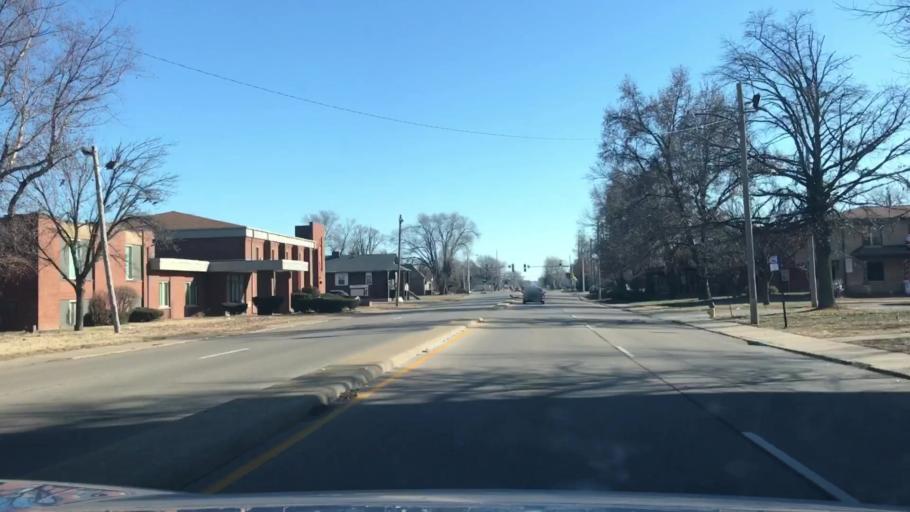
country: US
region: Illinois
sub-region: Saint Clair County
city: East Saint Louis
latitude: 38.6179
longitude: -90.1492
